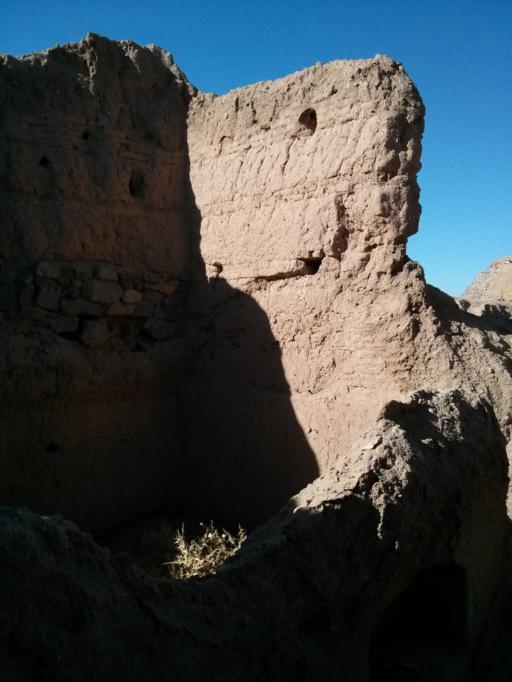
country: IR
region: Isfahan
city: Na'in
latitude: 32.6891
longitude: 52.8520
